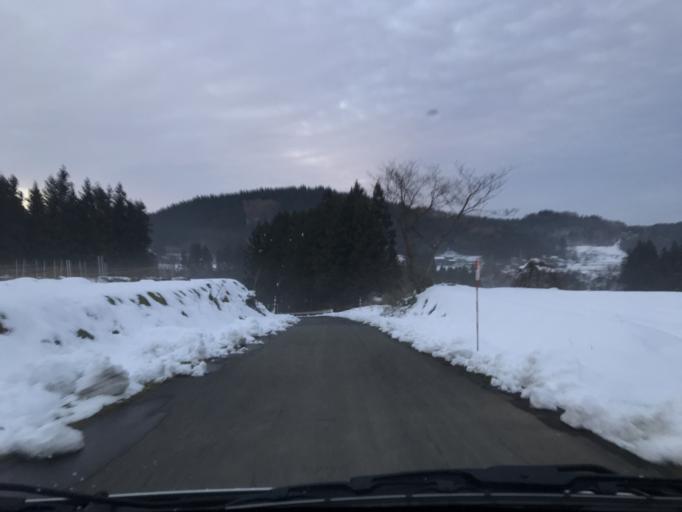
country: JP
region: Iwate
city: Mizusawa
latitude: 39.0569
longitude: 141.0329
